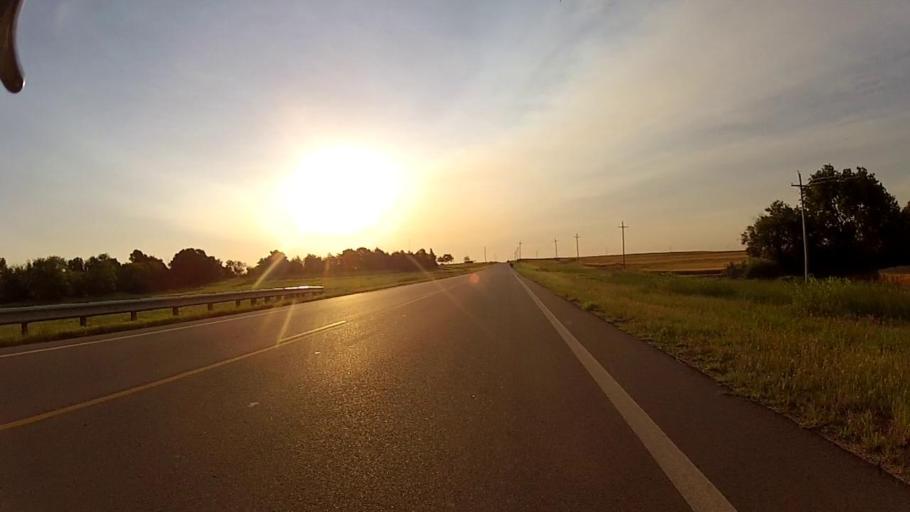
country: US
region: Kansas
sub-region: Harper County
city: Anthony
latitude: 37.1527
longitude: -97.9350
